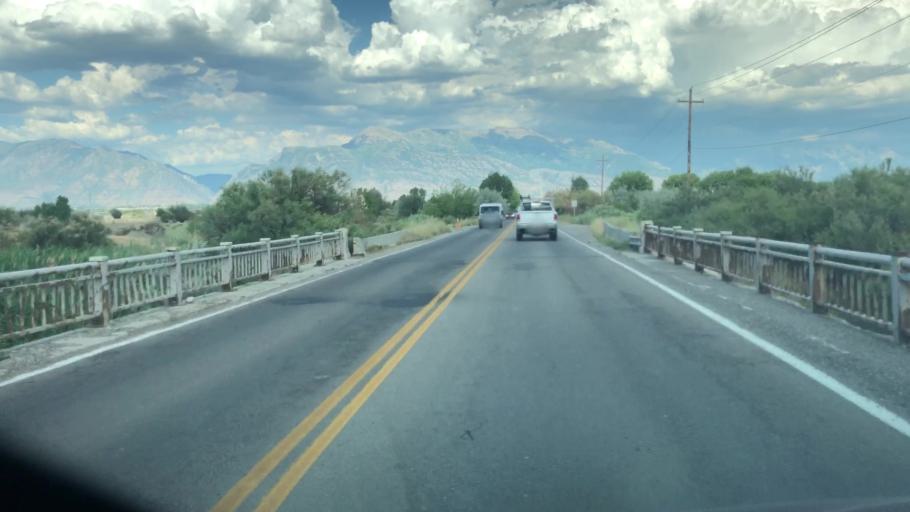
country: US
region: Utah
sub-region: Utah County
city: Saratoga Springs
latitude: 40.3874
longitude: -111.9055
